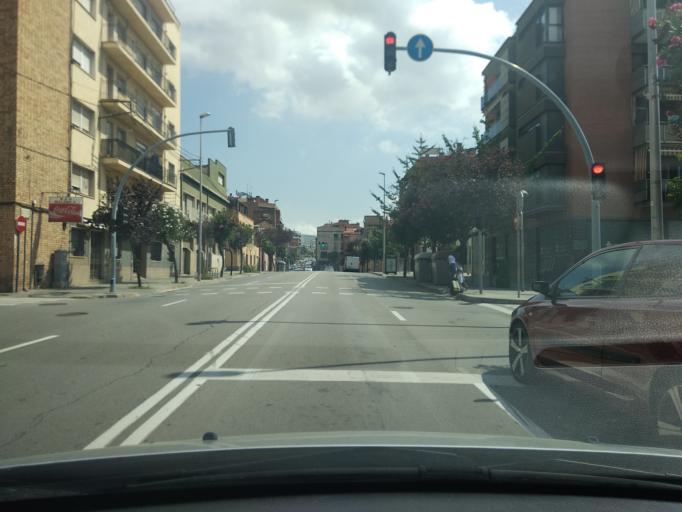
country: ES
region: Catalonia
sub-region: Provincia de Barcelona
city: Canovelles
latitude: 41.6139
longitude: 2.2886
